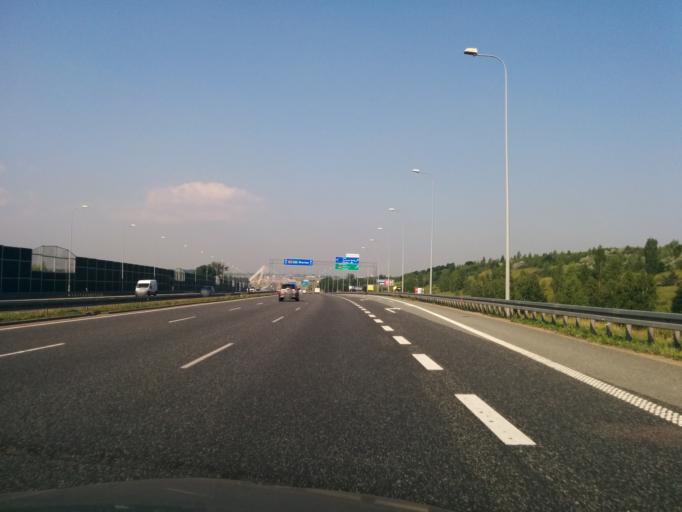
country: PL
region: Silesian Voivodeship
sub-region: Powiat gliwicki
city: Przyszowice
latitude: 50.2692
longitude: 18.7548
